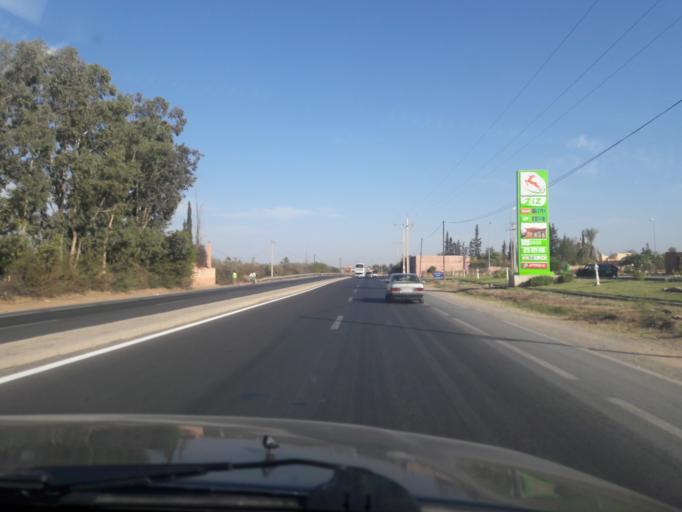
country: MA
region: Marrakech-Tensift-Al Haouz
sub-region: Marrakech
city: Marrakesh
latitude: 31.6472
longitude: -7.8987
